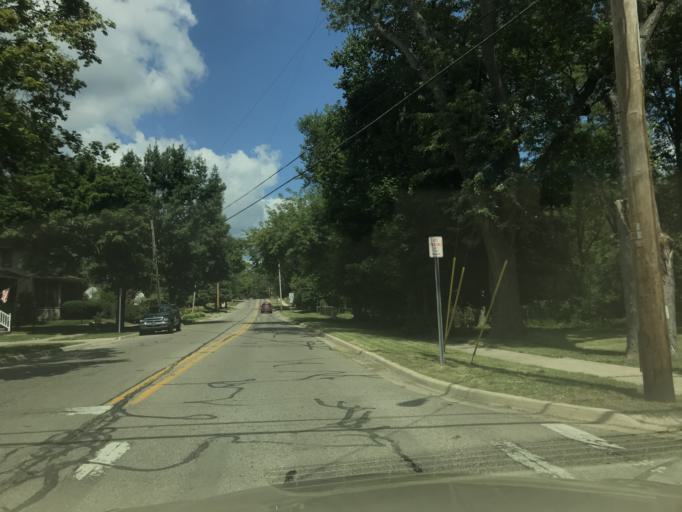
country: US
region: Michigan
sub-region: Jackson County
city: Jackson
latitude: 42.2328
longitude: -84.4184
